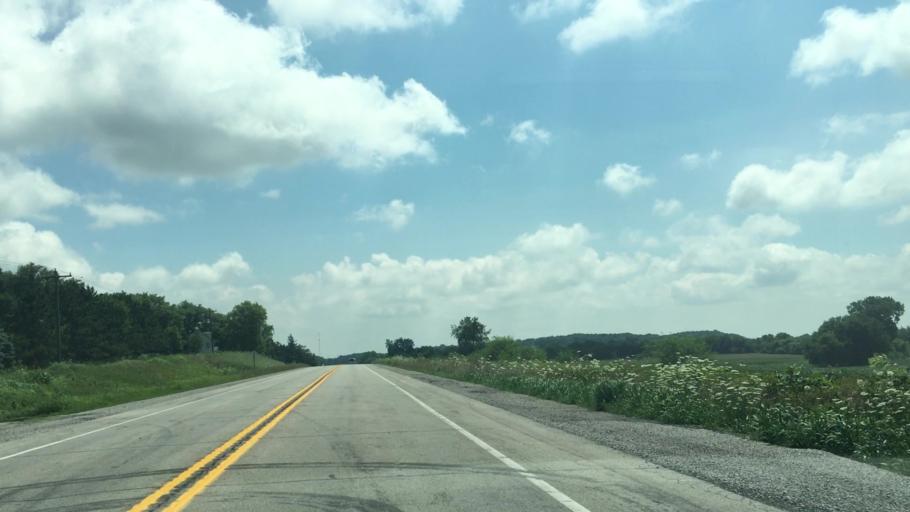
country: US
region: Iowa
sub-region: Johnson County
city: Tiffin
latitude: 41.7157
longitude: -91.7237
